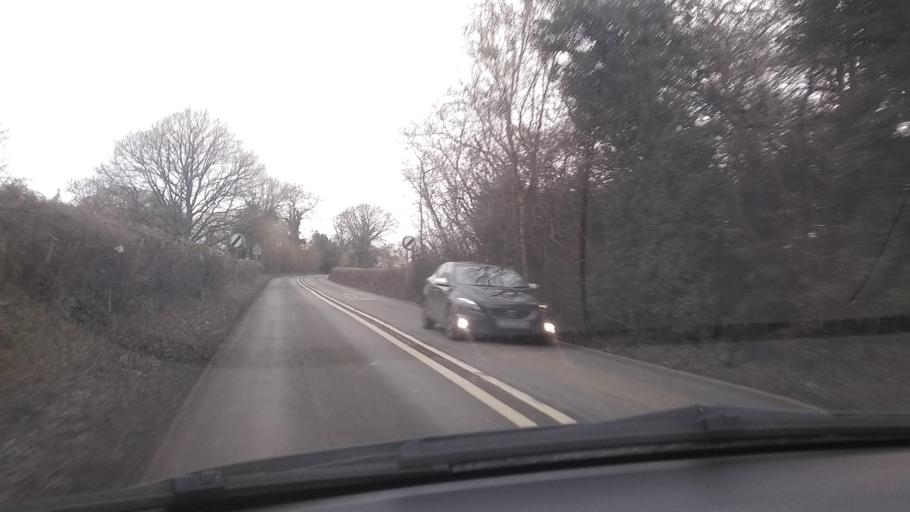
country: GB
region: England
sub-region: Shropshire
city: Cleobury Mortimer
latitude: 52.3836
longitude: -2.5375
